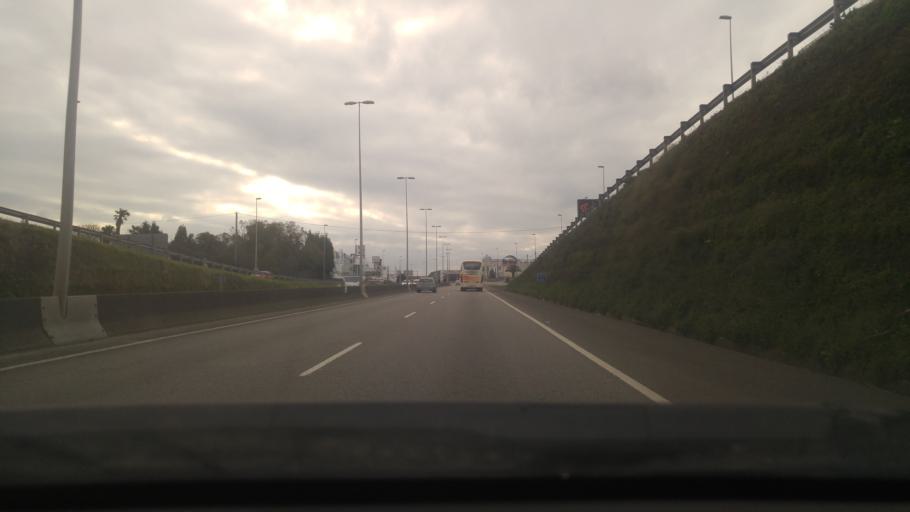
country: ES
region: Asturias
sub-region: Province of Asturias
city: Natahoyo
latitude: 43.5097
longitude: -5.6914
